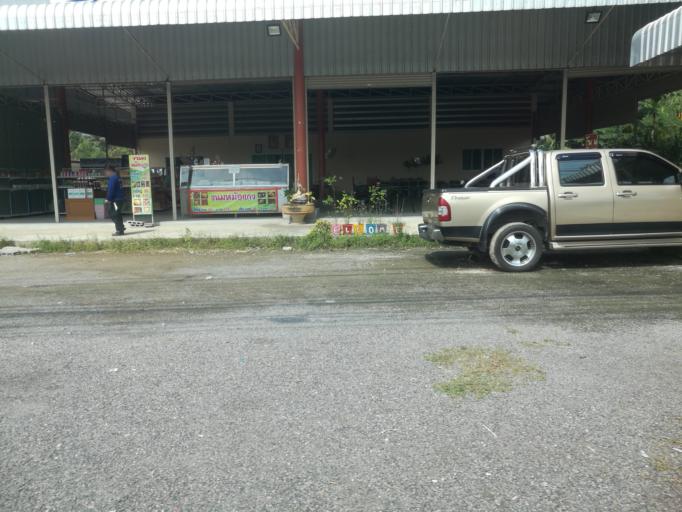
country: TH
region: Samut Songkhram
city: Amphawa
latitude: 13.3702
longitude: 99.9567
